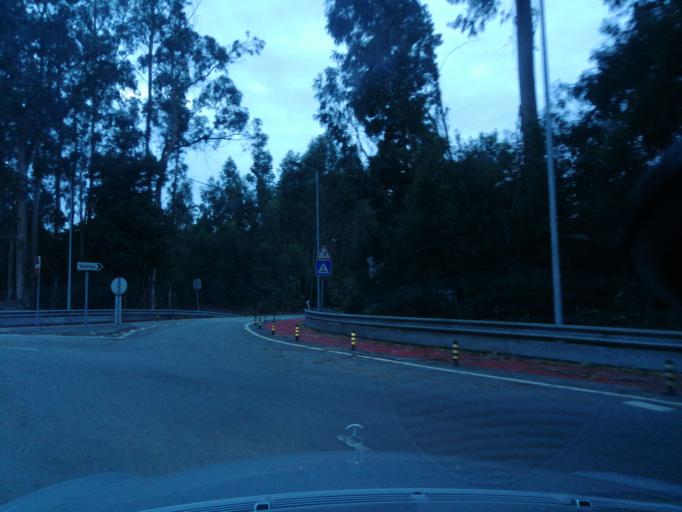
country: PT
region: Aveiro
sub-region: Estarreja
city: Estarreja
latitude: 40.7592
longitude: -8.6036
